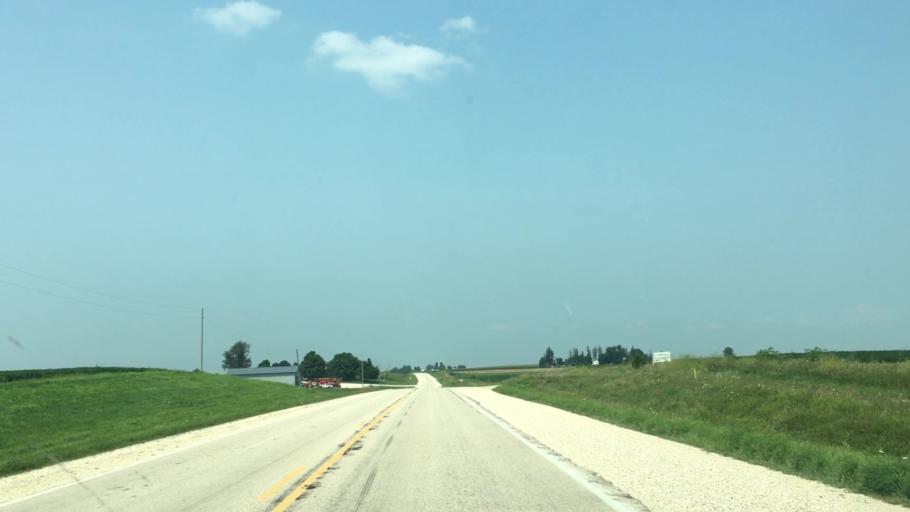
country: US
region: Iowa
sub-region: Fayette County
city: West Union
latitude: 42.9882
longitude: -91.8241
